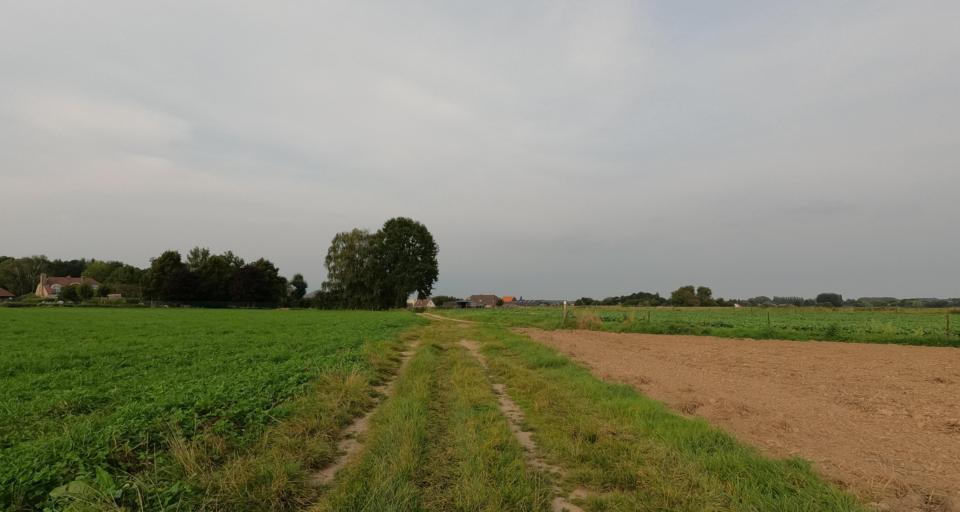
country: BE
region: Flanders
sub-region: Provincie Vlaams-Brabant
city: Wemmel
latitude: 50.9412
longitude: 4.2829
